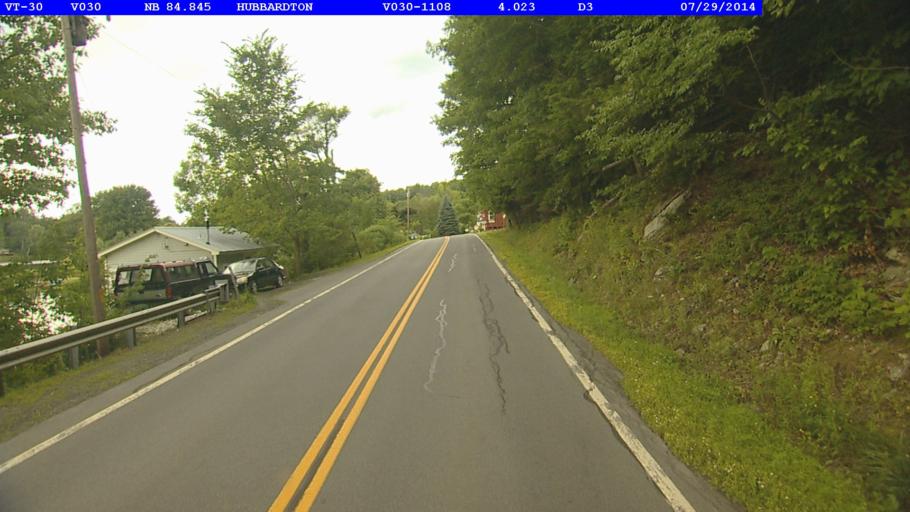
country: US
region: Vermont
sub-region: Rutland County
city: Brandon
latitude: 43.7354
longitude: -73.1802
